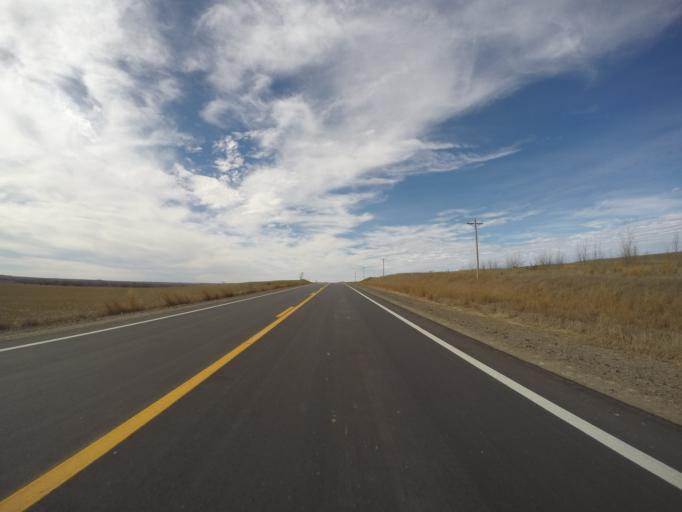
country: US
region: Nebraska
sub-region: Franklin County
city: Franklin
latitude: 40.0962
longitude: -98.8643
